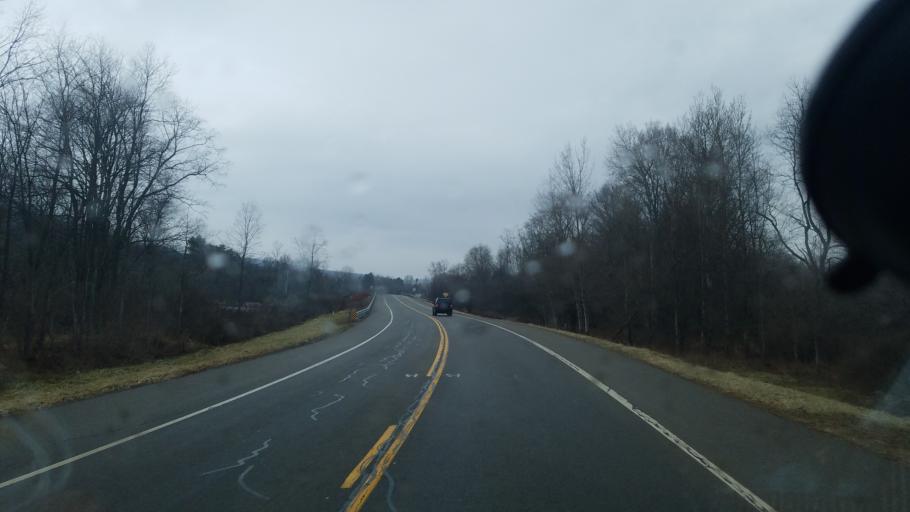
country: US
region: New York
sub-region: Allegany County
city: Wellsville
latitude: 42.0130
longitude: -77.8916
